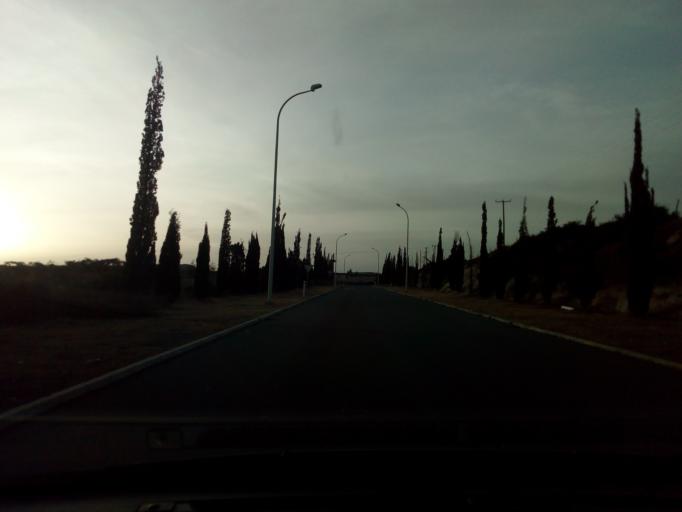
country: CY
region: Limassol
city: Pyrgos
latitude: 34.7317
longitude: 33.2853
